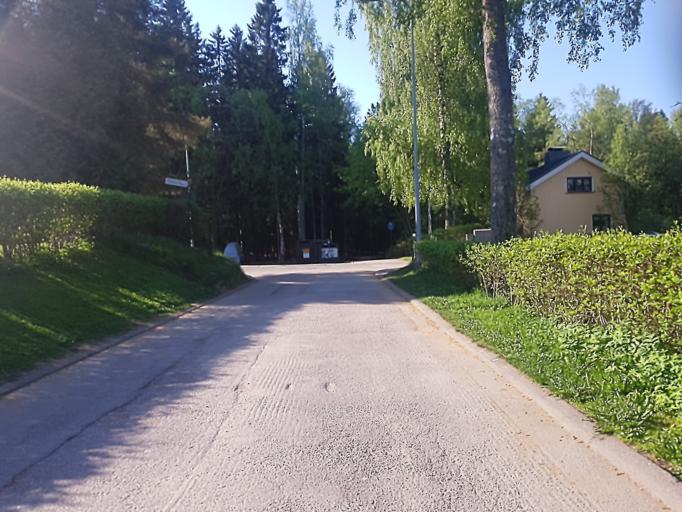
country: FI
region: Uusimaa
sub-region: Helsinki
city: Helsinki
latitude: 60.2441
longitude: 24.9331
